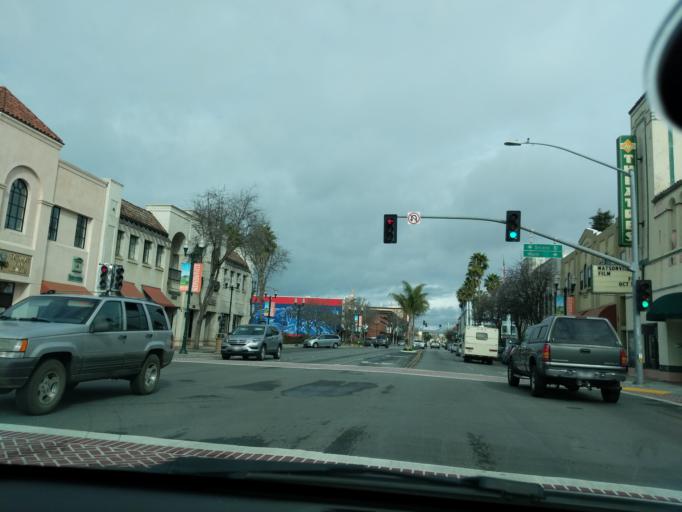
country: US
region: California
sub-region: Santa Cruz County
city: Watsonville
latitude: 36.9091
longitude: -121.7556
